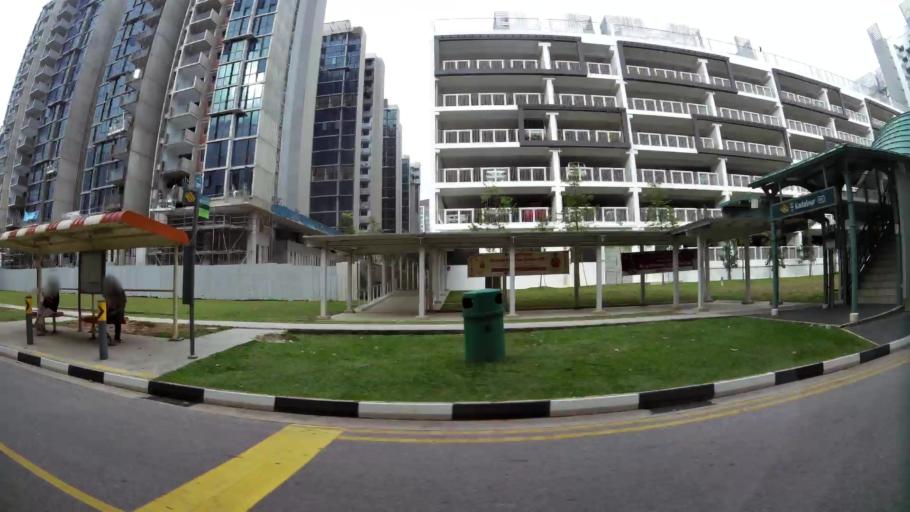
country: MY
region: Johor
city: Kampung Pasir Gudang Baru
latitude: 1.3998
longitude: 103.9164
